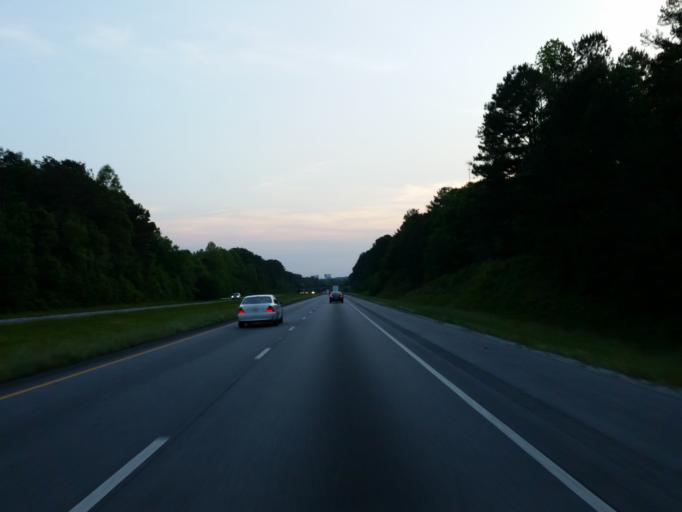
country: US
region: Alabama
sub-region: Cleburne County
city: Heflin
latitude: 33.6249
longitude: -85.5696
